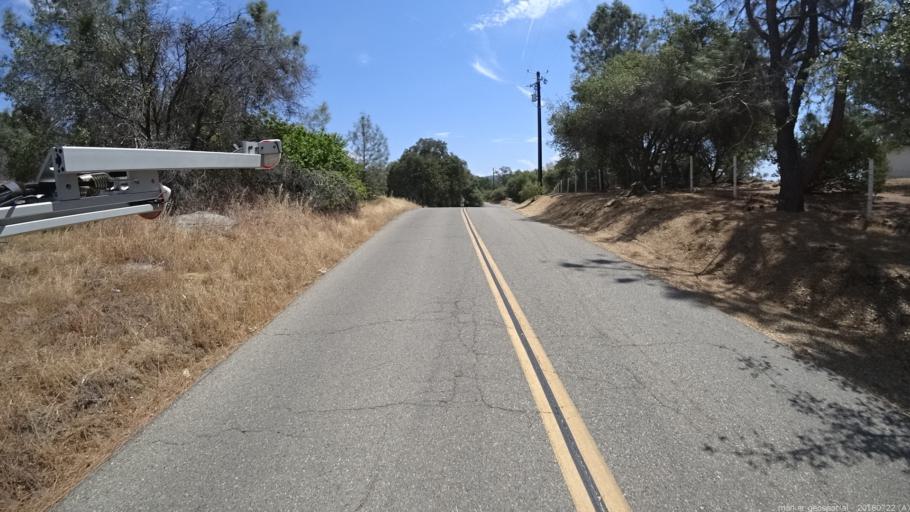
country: US
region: California
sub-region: Madera County
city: Coarsegold
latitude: 37.2768
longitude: -119.7429
